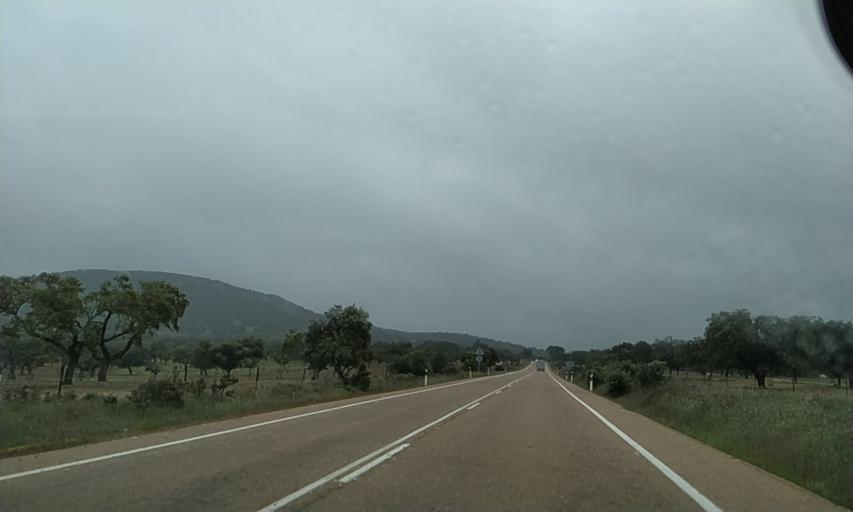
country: ES
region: Extremadura
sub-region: Provincia de Badajoz
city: Puebla de Obando
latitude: 39.2082
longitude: -6.5859
